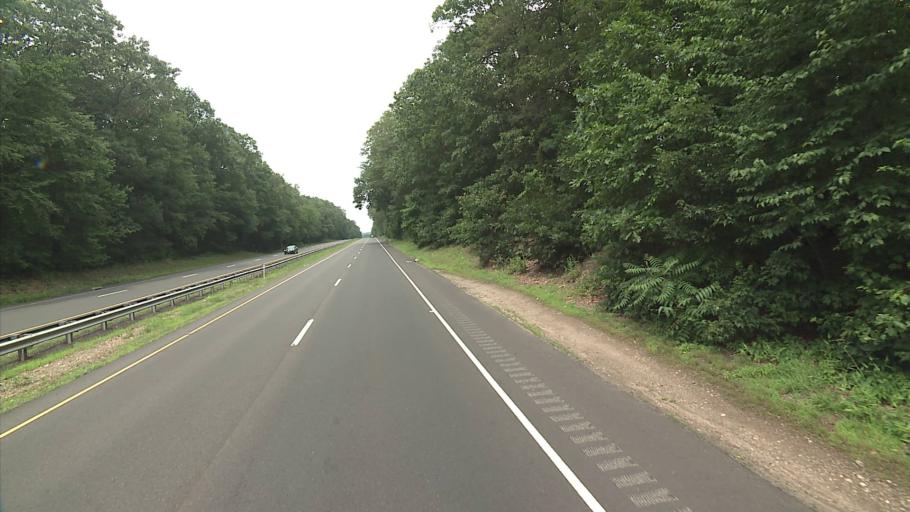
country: US
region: Connecticut
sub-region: New Haven County
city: Madison
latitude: 41.2819
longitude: -72.5653
